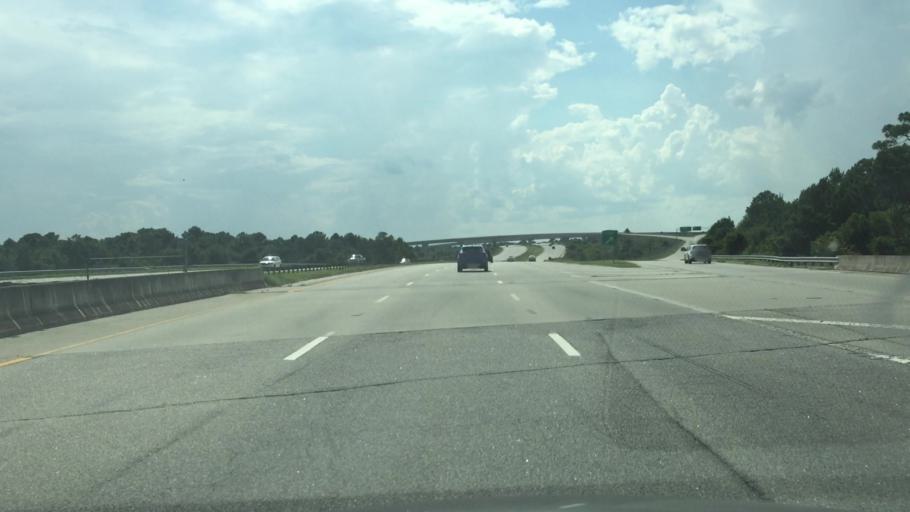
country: US
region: South Carolina
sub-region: Horry County
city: North Myrtle Beach
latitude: 33.8115
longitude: -78.7702
